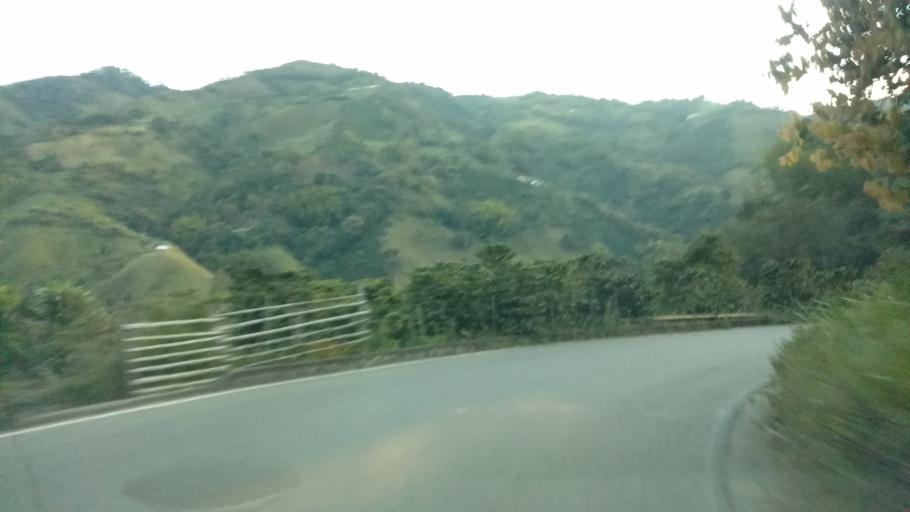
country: CO
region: Caldas
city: Aranzazu
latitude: 5.2582
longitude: -75.4979
